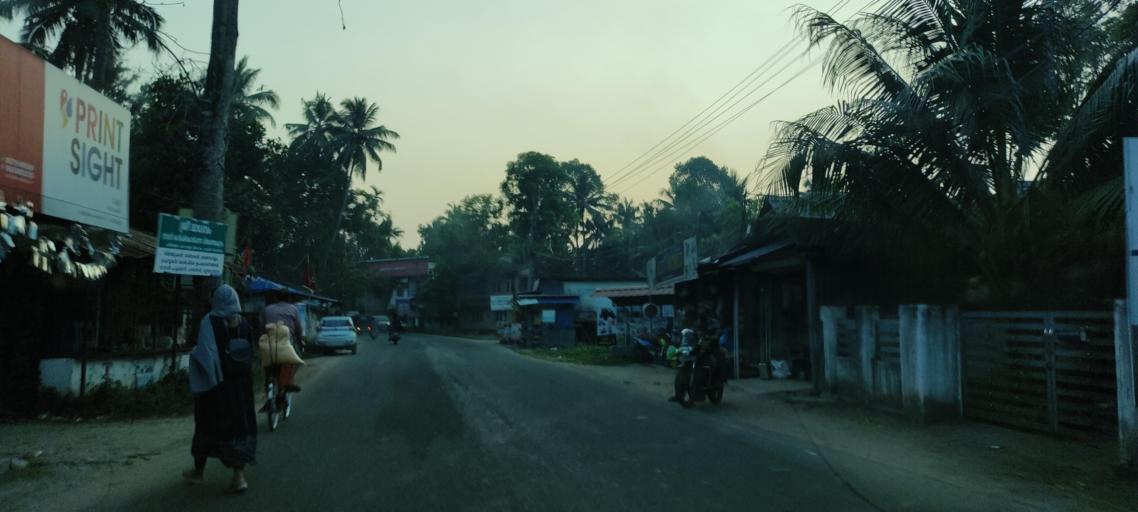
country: IN
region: Kerala
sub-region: Alappuzha
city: Kayankulam
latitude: 9.1331
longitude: 76.5065
